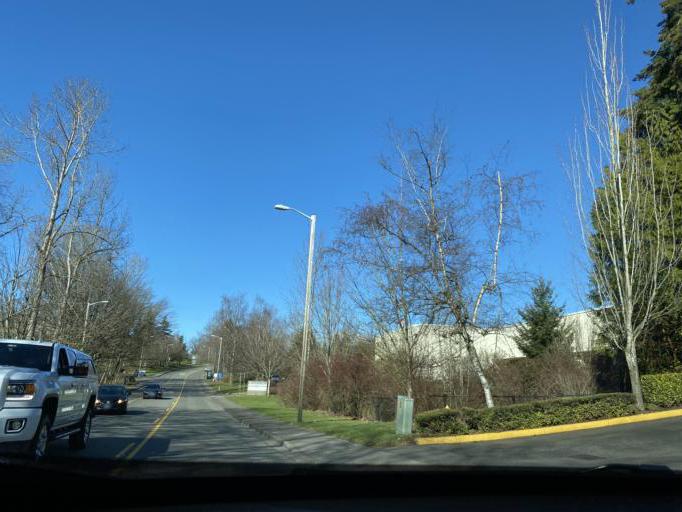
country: US
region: Washington
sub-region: King County
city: Federal Way
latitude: 47.2907
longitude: -122.3230
